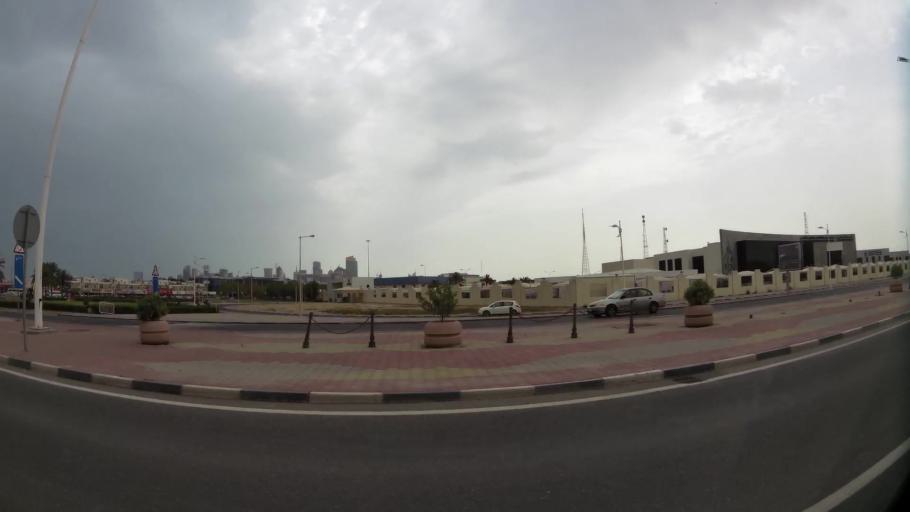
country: QA
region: Baladiyat ad Dawhah
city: Doha
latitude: 25.3164
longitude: 51.4954
